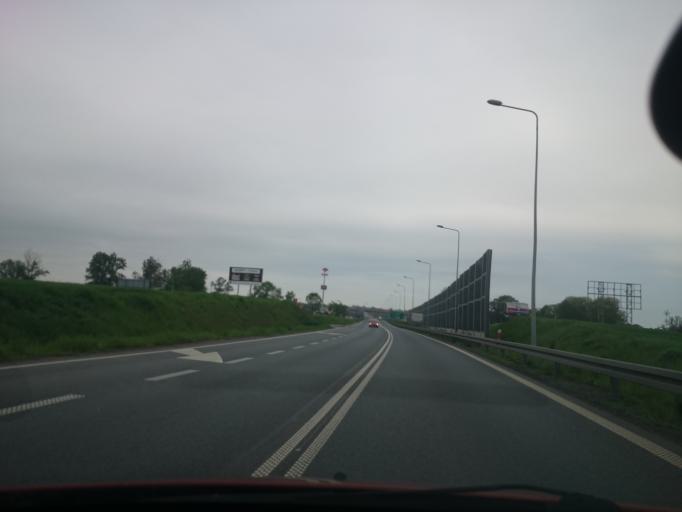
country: PL
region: Opole Voivodeship
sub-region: Powiat opolski
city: Czarnowasy
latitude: 50.7038
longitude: 17.9106
